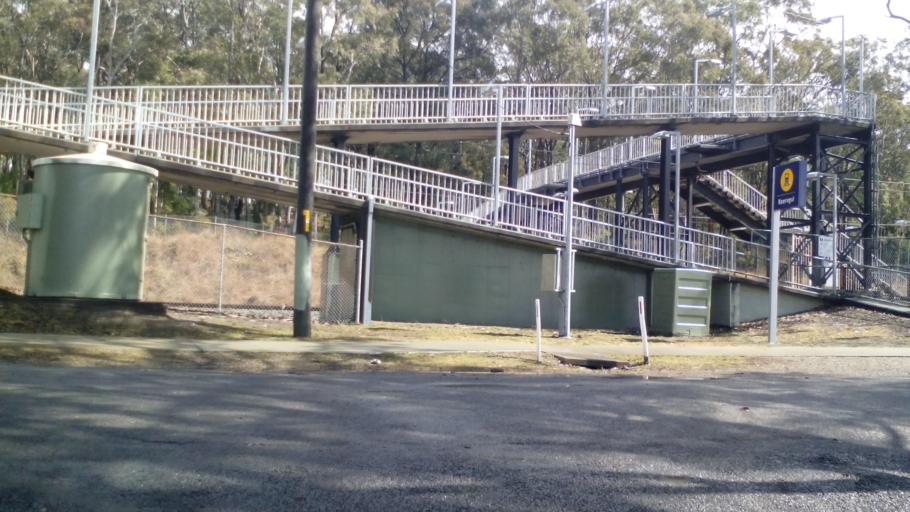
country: AU
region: New South Wales
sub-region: Lake Macquarie Shire
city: Fennell Bay
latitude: -32.9717
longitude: 151.6055
